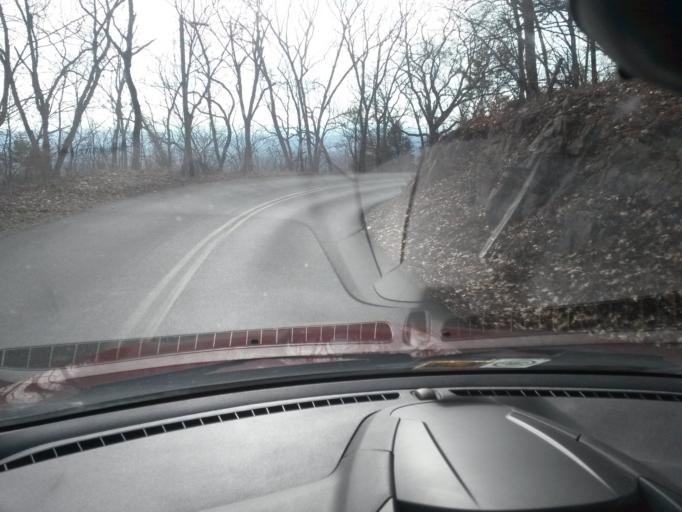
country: US
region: Virginia
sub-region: Botetourt County
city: Fincastle
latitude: 37.5554
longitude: -79.8739
